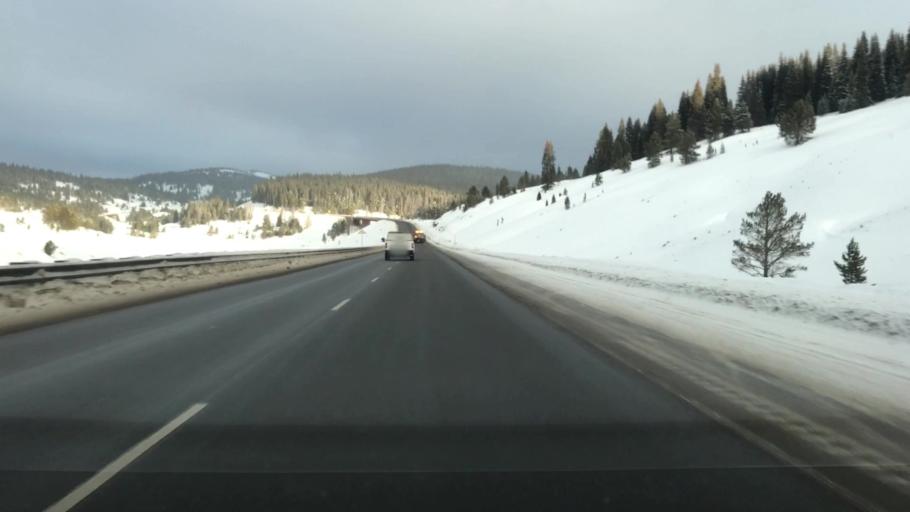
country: US
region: Colorado
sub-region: Summit County
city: Frisco
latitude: 39.5100
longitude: -106.2024
